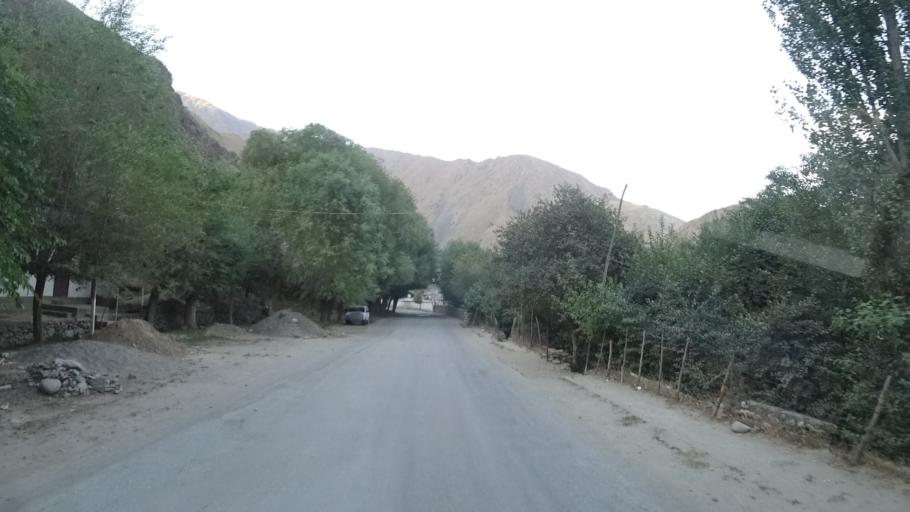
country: AF
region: Badakhshan
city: Nusay
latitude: 38.4485
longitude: 70.8179
